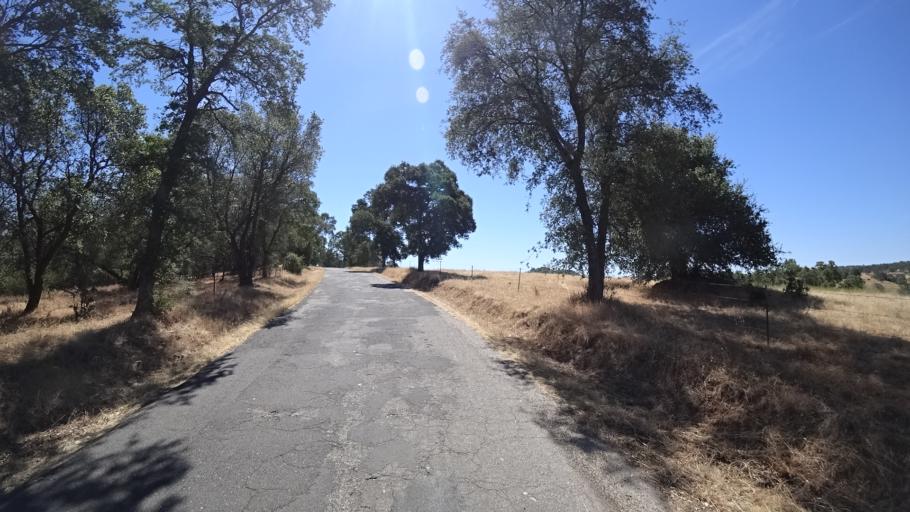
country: US
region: California
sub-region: Calaveras County
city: Angels Camp
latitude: 38.1199
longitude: -120.5727
